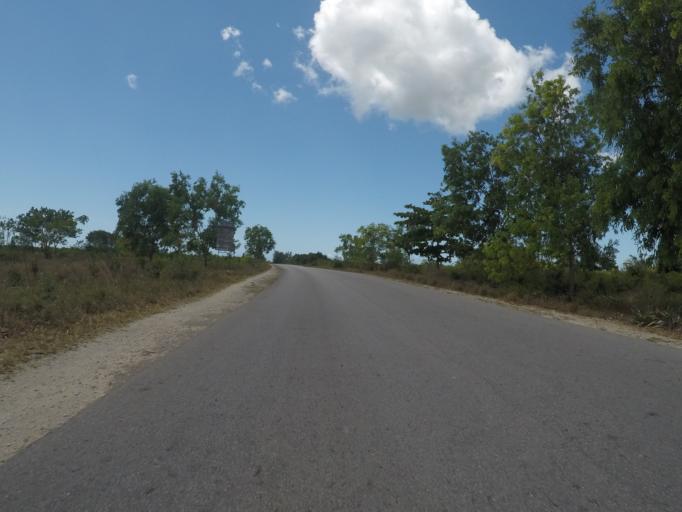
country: TZ
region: Zanzibar Central/South
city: Nganane
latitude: -6.2821
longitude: 39.4717
